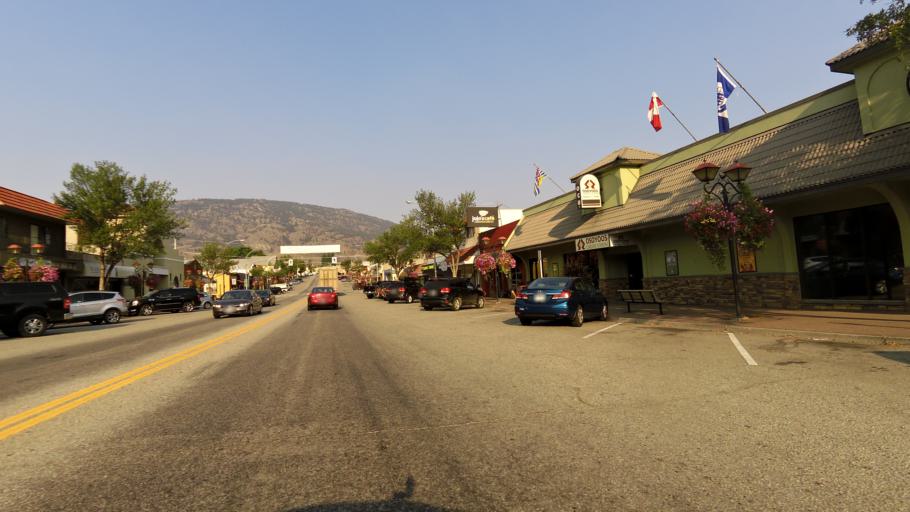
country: CA
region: British Columbia
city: Osoyoos
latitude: 49.0330
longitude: -119.4642
